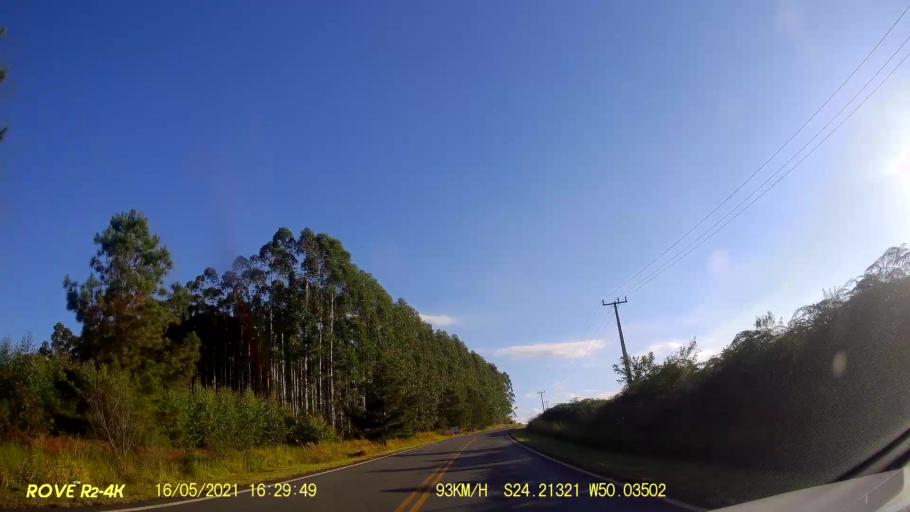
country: BR
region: Parana
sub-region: Pirai Do Sul
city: Pirai do Sul
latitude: -24.2134
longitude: -50.0352
